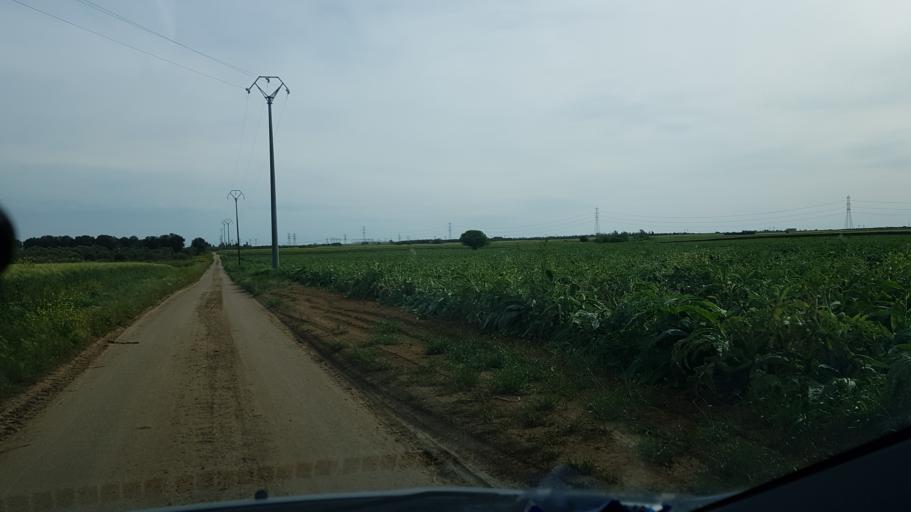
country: IT
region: Apulia
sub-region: Provincia di Brindisi
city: Tuturano
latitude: 40.5768
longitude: 17.9212
